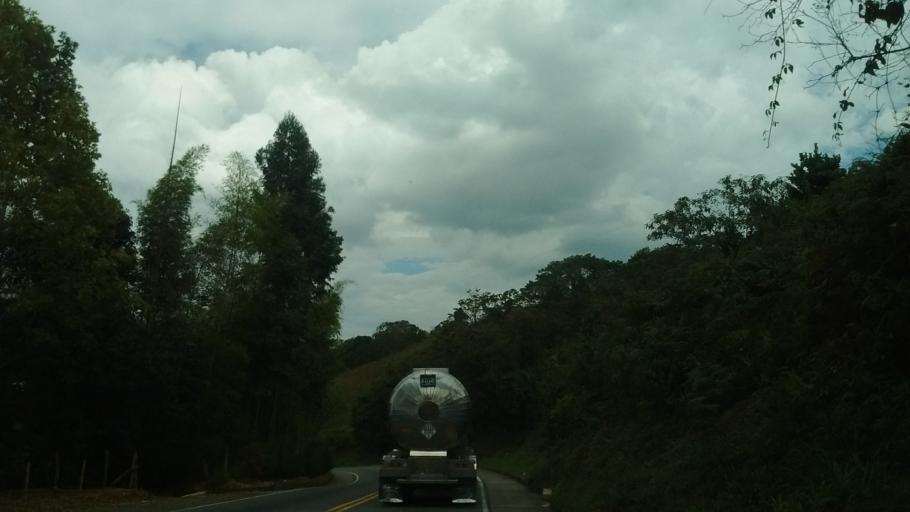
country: CO
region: Cauca
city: Rosas
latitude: 2.3099
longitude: -76.6891
